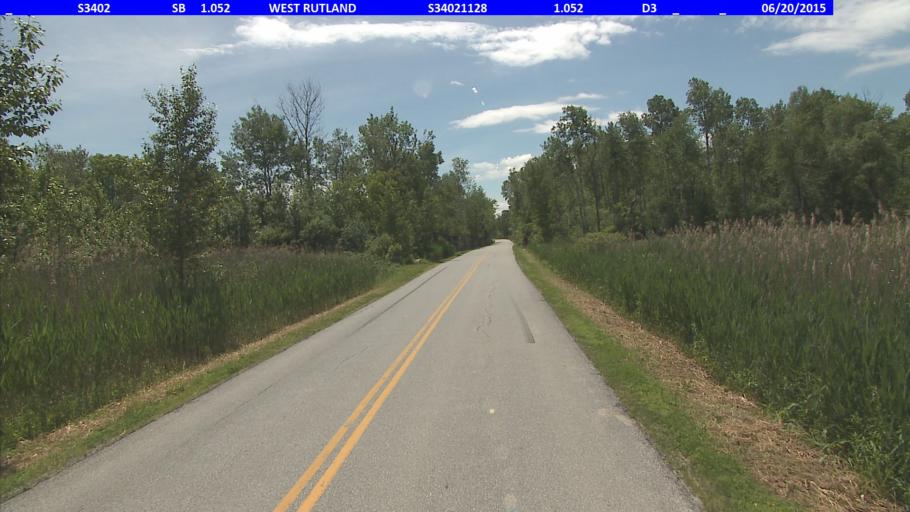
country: US
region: Vermont
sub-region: Rutland County
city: West Rutland
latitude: 43.6085
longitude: -73.0558
